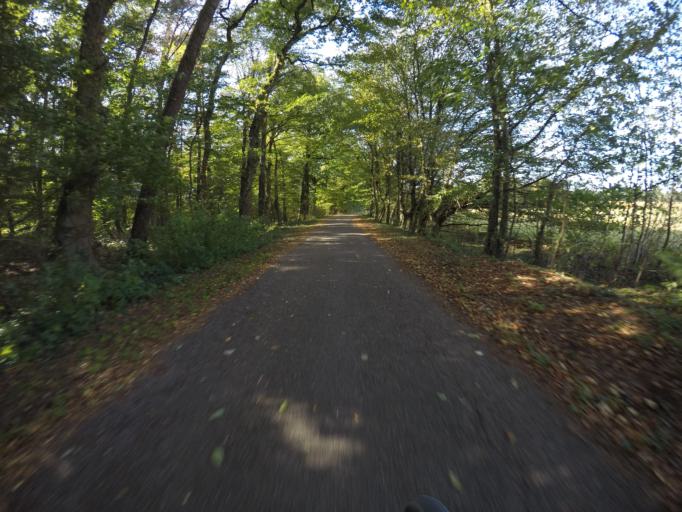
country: DE
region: Baden-Wuerttemberg
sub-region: Karlsruhe Region
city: Kronau
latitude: 49.2341
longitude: 8.6179
